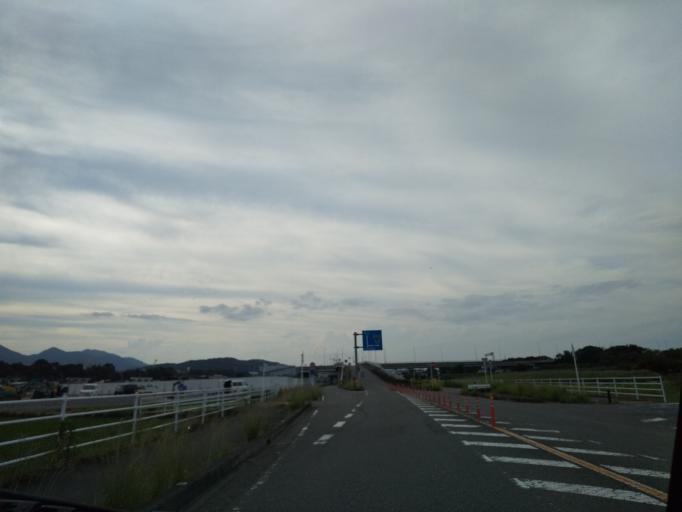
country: JP
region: Kanagawa
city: Zama
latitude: 35.4802
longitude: 139.3565
